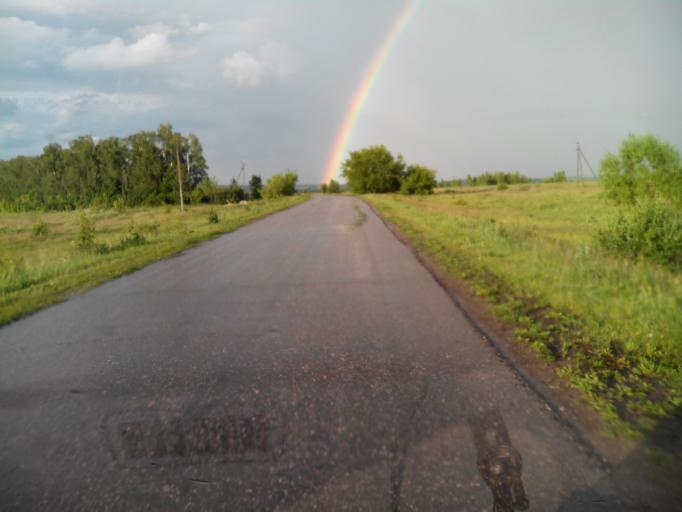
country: RU
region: Penza
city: Zasechnoye
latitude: 53.0595
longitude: 44.9843
